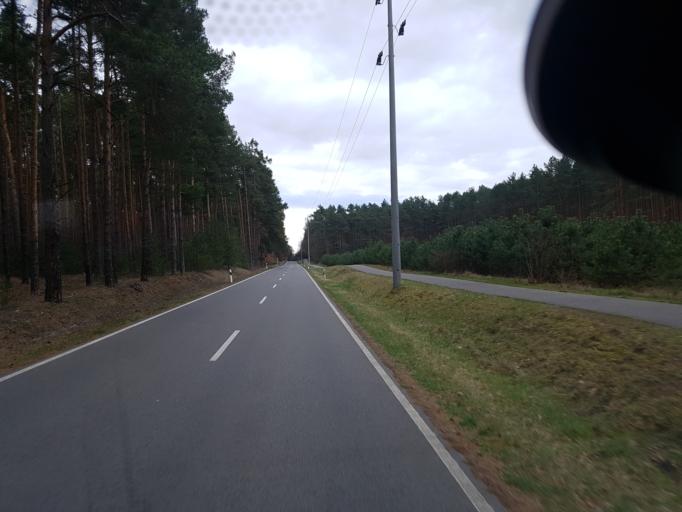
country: DE
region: Brandenburg
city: Mixdorf
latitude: 52.1893
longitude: 14.4250
